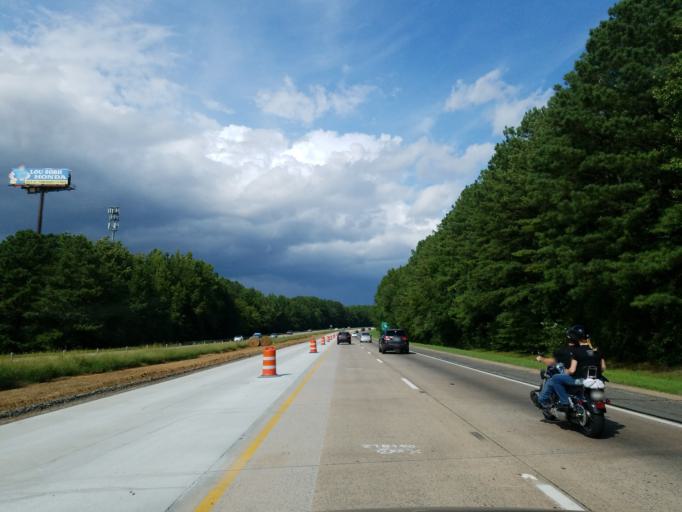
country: US
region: Georgia
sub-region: Forsyth County
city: Cumming
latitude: 34.1515
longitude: -84.1866
